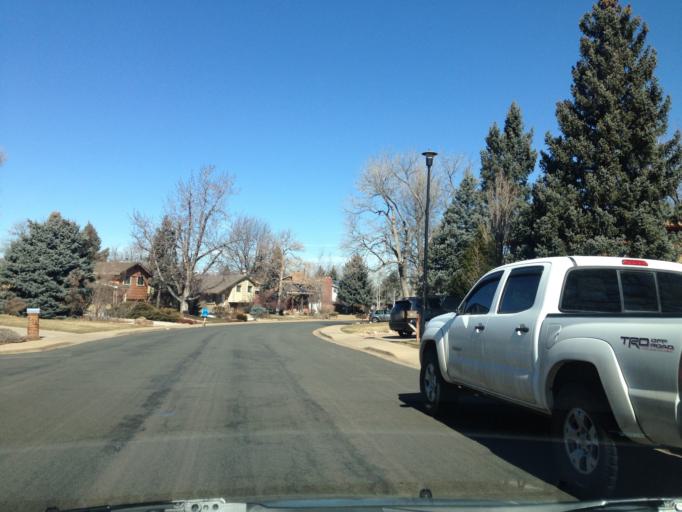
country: US
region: Colorado
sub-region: Boulder County
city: Boulder
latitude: 39.9906
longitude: -105.2286
